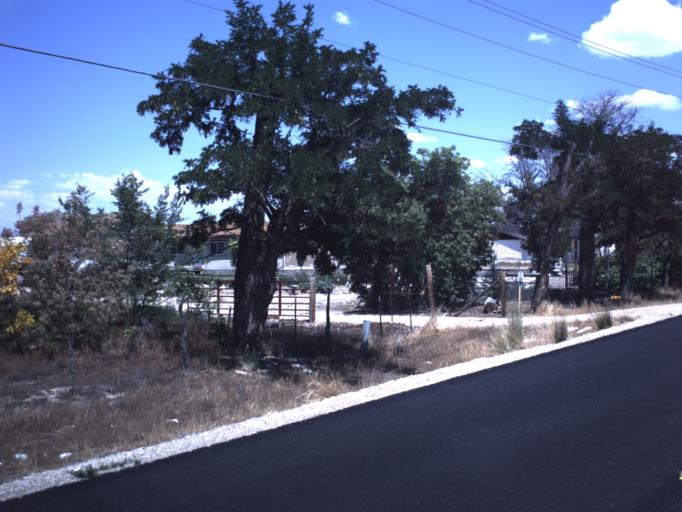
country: US
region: Utah
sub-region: Emery County
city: Orangeville
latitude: 39.2279
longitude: -111.0356
